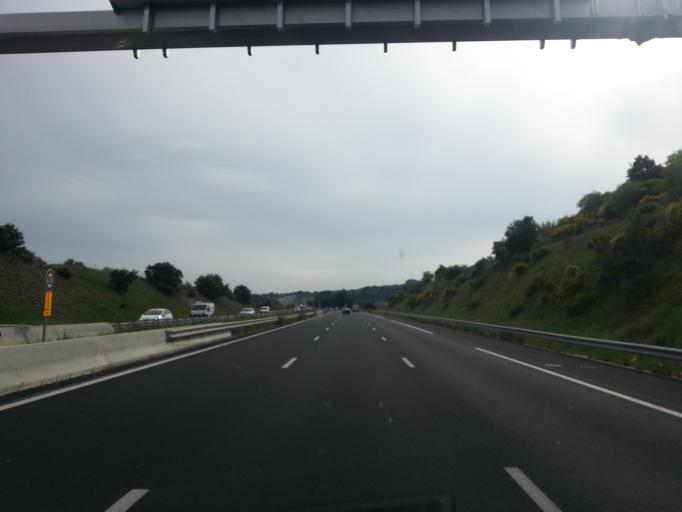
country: FR
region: Languedoc-Roussillon
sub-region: Departement du Gard
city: Tavel
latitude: 44.0128
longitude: 4.7170
